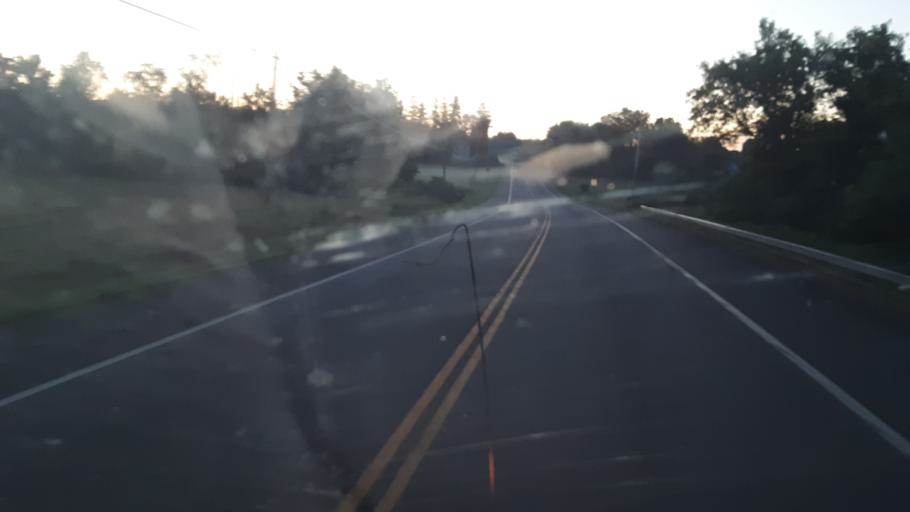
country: US
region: New York
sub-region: Montgomery County
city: Hagaman
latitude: 42.9470
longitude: -74.1372
